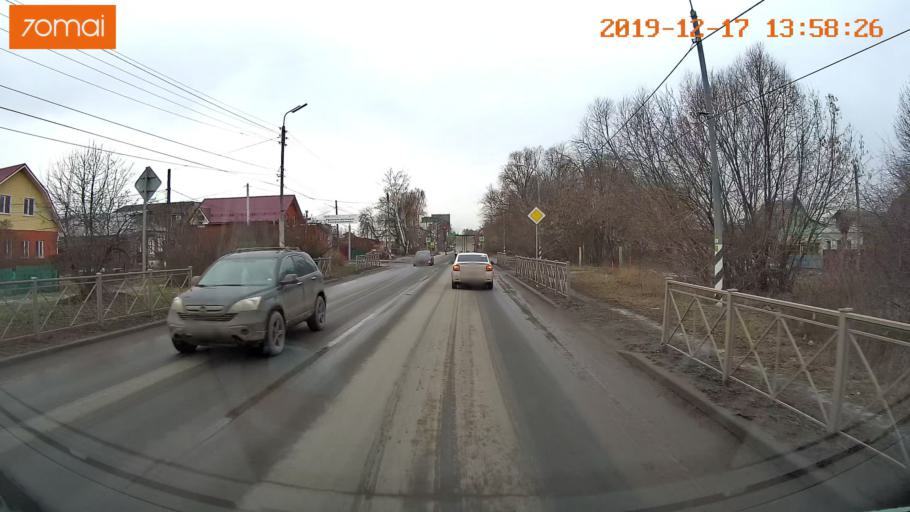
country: RU
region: Rjazan
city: Ryazan'
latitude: 54.6231
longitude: 39.6841
